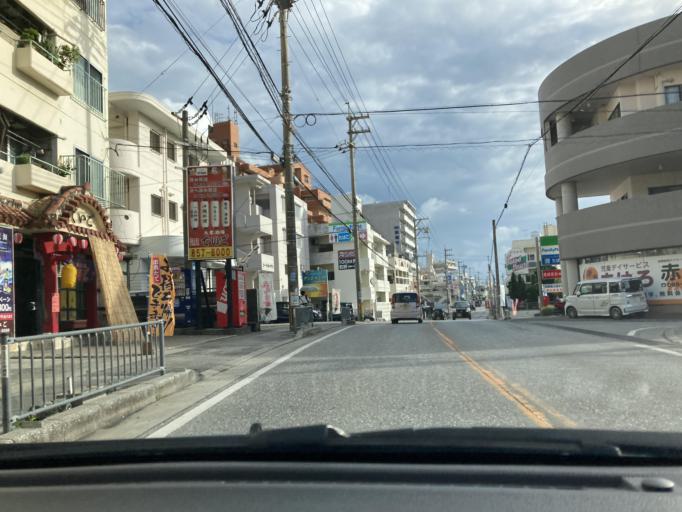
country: JP
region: Okinawa
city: Tomigusuku
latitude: 26.1898
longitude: 127.6604
